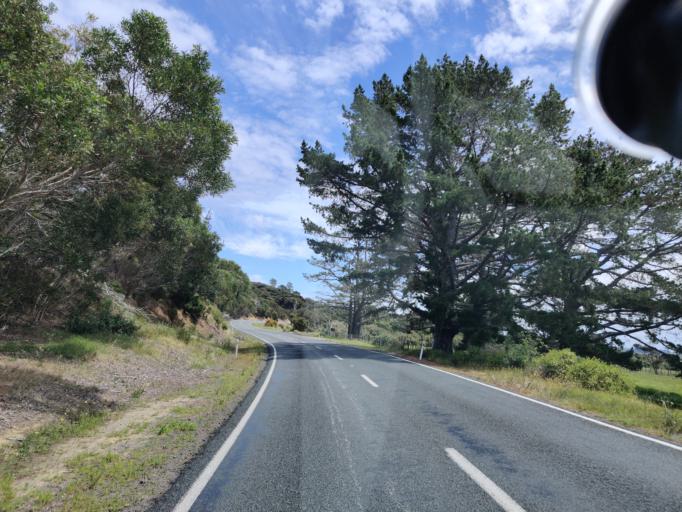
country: NZ
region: Northland
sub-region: Far North District
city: Kaitaia
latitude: -34.8044
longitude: 173.1138
